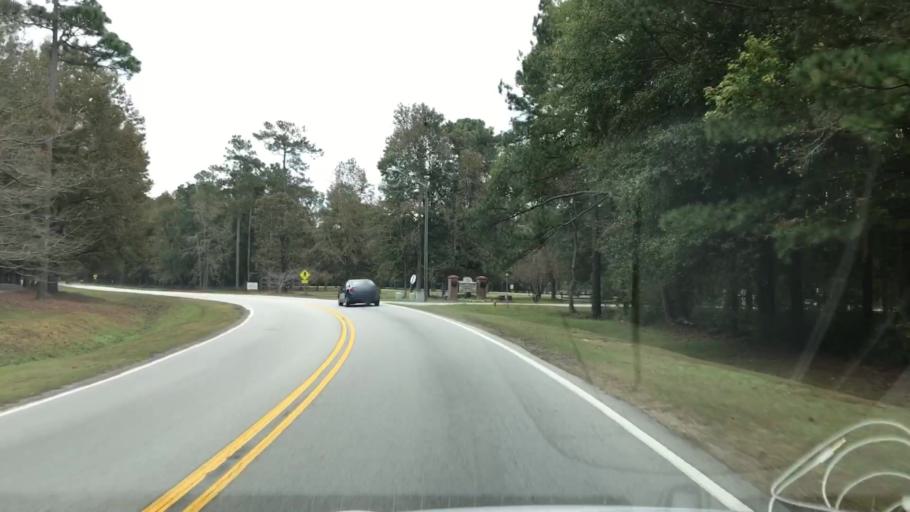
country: US
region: South Carolina
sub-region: Berkeley County
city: Goose Creek
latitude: 33.0088
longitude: -80.0585
